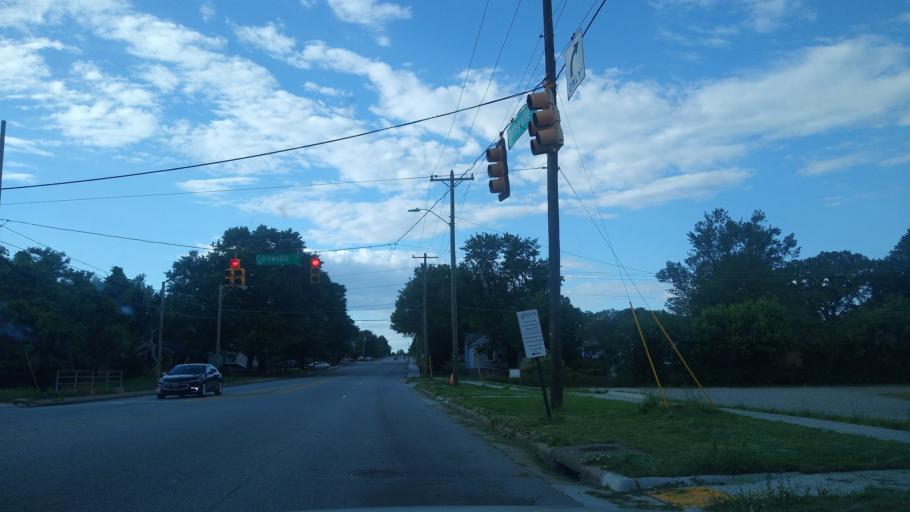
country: US
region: North Carolina
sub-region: Guilford County
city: Greensboro
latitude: 36.1016
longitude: -79.7752
